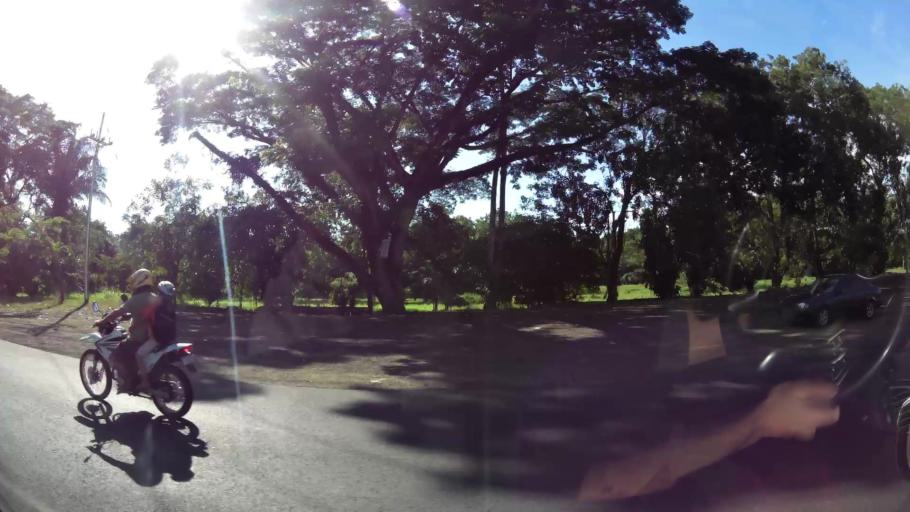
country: CR
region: Puntarenas
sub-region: Canton de Garabito
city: Jaco
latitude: 9.6041
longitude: -84.6156
